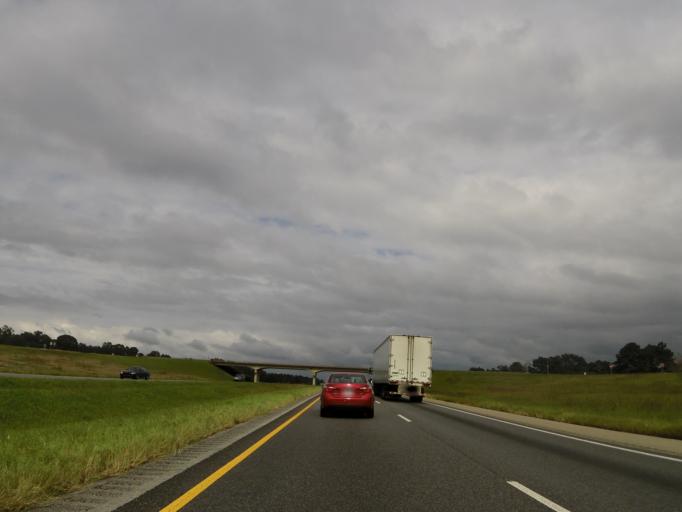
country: US
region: Alabama
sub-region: Escambia County
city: Brewton
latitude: 31.2751
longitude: -87.2065
